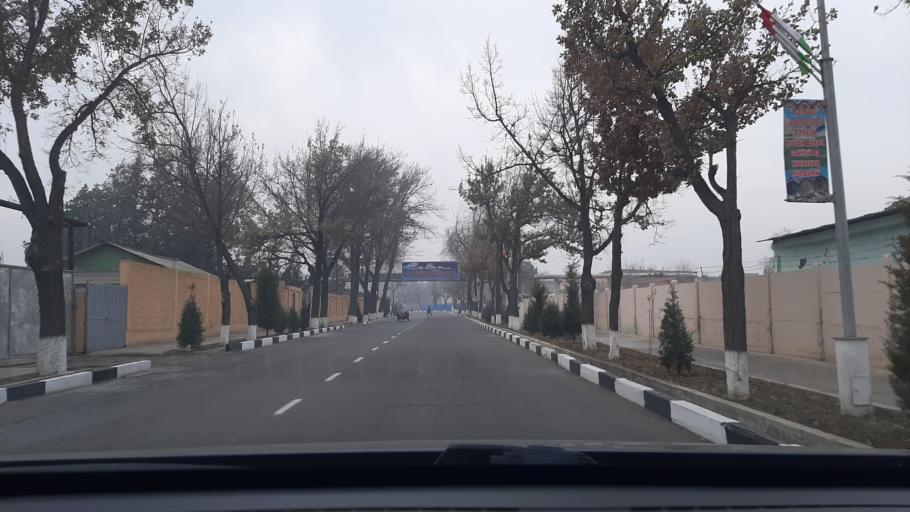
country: TJ
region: Viloyati Sughd
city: Chkalov
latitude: 40.2374
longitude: 69.6890
